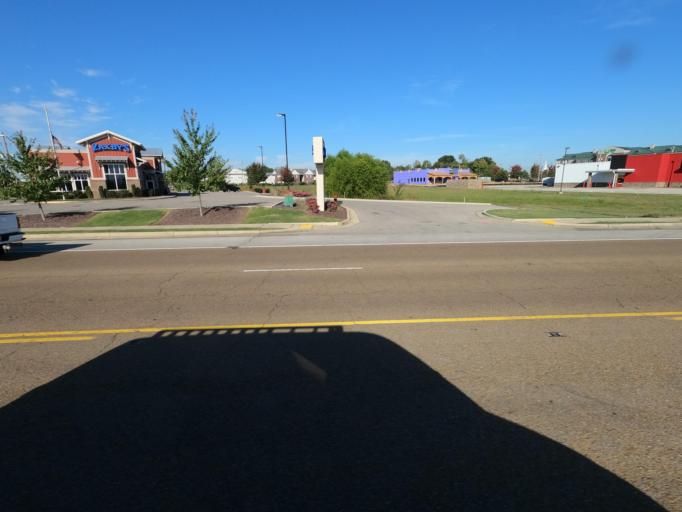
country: US
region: Tennessee
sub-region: Shelby County
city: Millington
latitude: 35.3596
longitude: -89.8925
